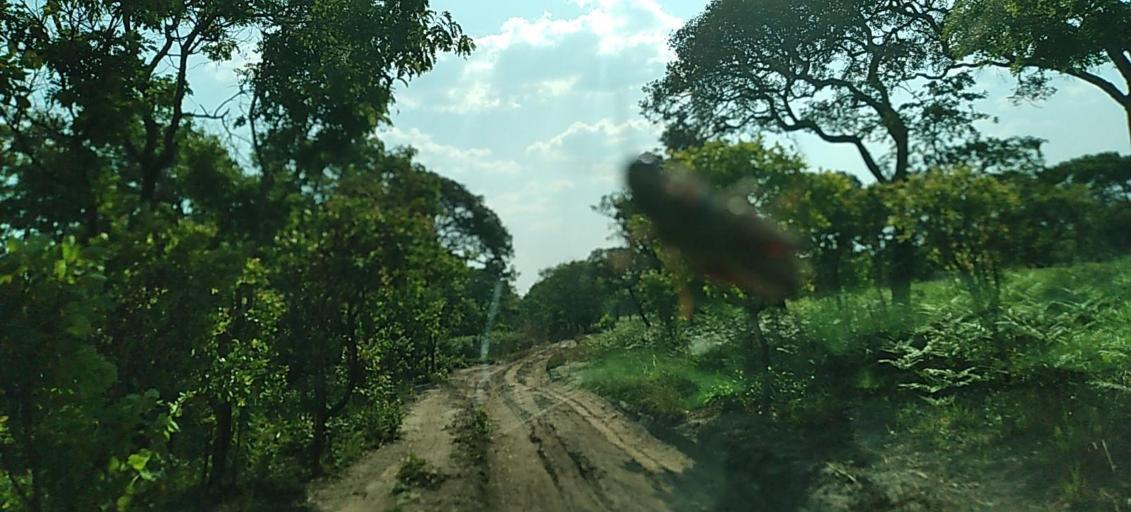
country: ZM
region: North-Western
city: Mwinilunga
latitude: -11.3087
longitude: 24.7848
